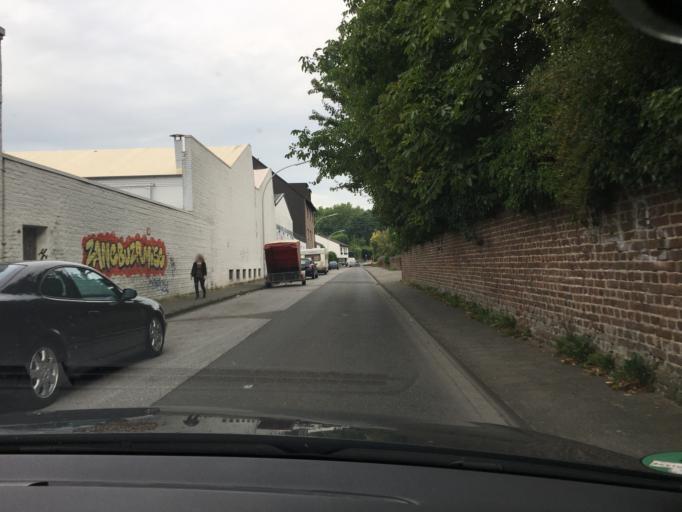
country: DE
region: North Rhine-Westphalia
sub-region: Regierungsbezirk Dusseldorf
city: Monchengladbach
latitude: 51.1326
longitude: 6.4140
